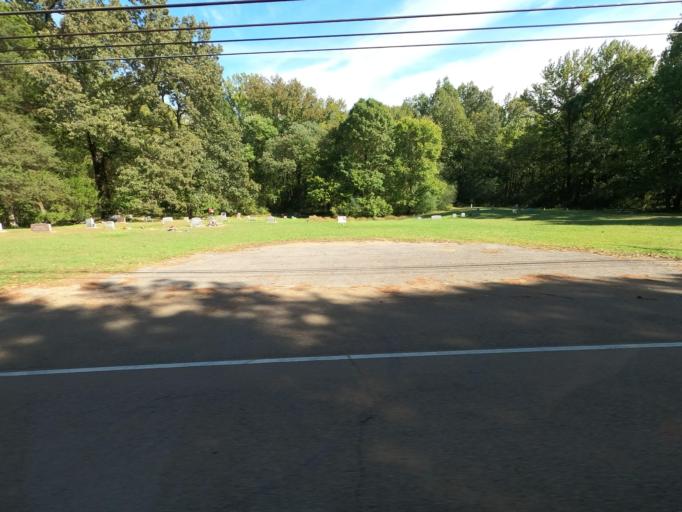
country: US
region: Tennessee
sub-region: Shelby County
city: Arlington
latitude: 35.2402
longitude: -89.6498
